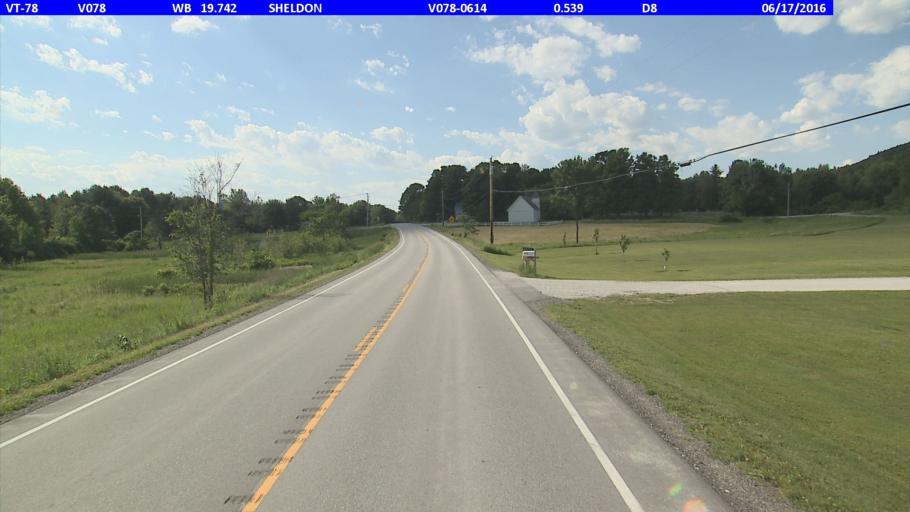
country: US
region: Vermont
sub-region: Franklin County
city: Enosburg Falls
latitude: 44.9181
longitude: -72.9620
